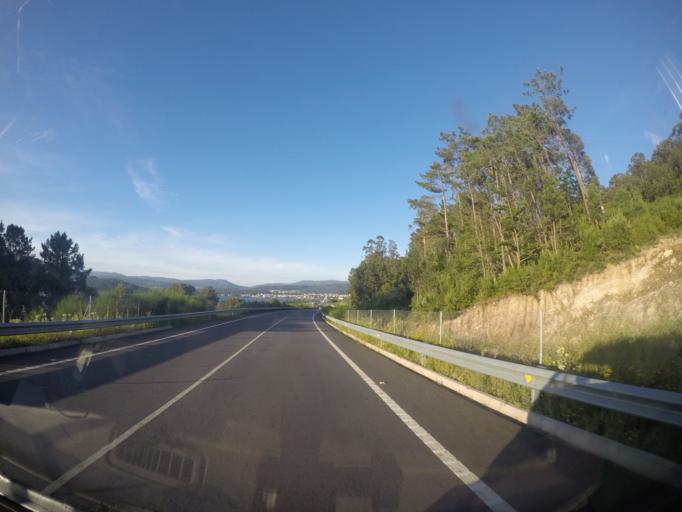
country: ES
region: Galicia
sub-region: Provincia da Coruna
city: Noia
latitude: 42.7851
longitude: -8.9205
